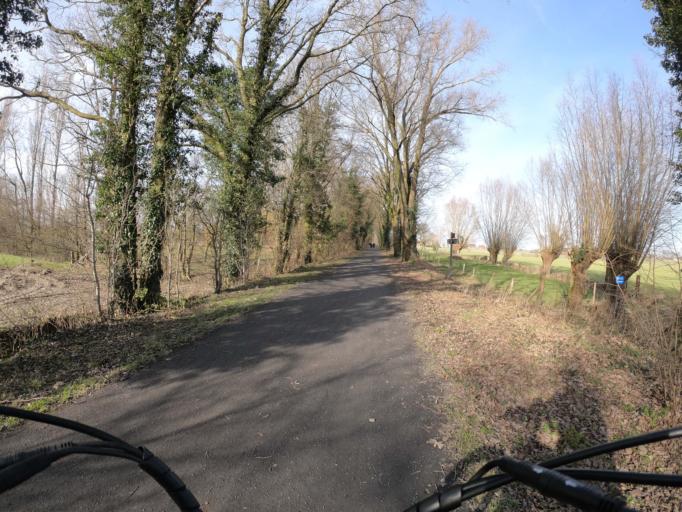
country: BE
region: Flanders
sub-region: Provincie West-Vlaanderen
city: Ledegem
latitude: 50.8853
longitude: 3.1267
